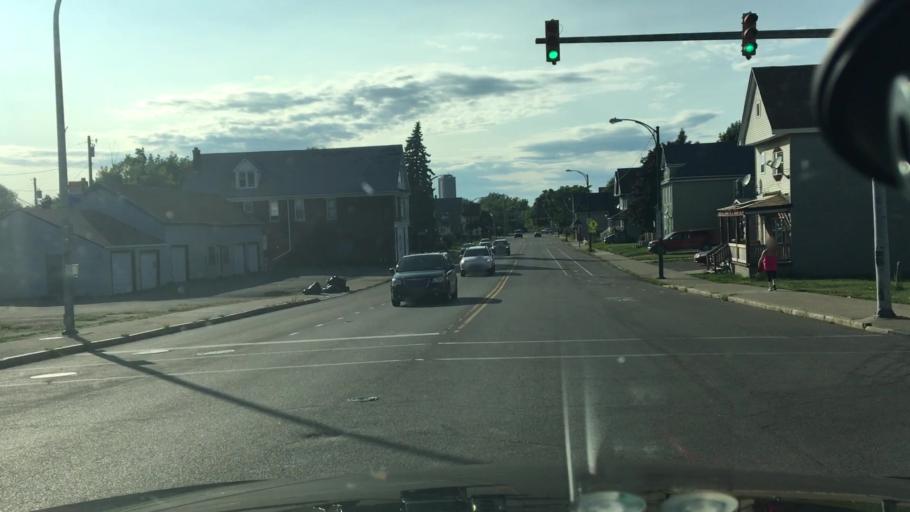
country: US
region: New York
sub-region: Erie County
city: Buffalo
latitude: 42.8661
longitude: -78.8477
